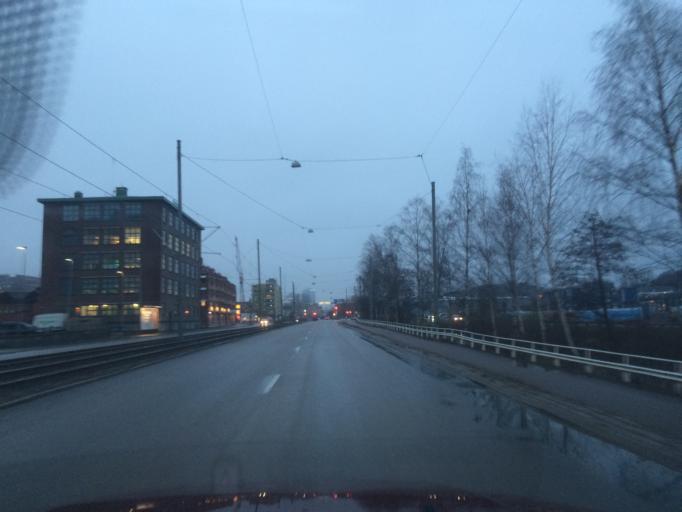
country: SE
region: Vaestra Goetaland
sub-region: Molndal
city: Moelndal
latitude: 57.6818
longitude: 12.0018
